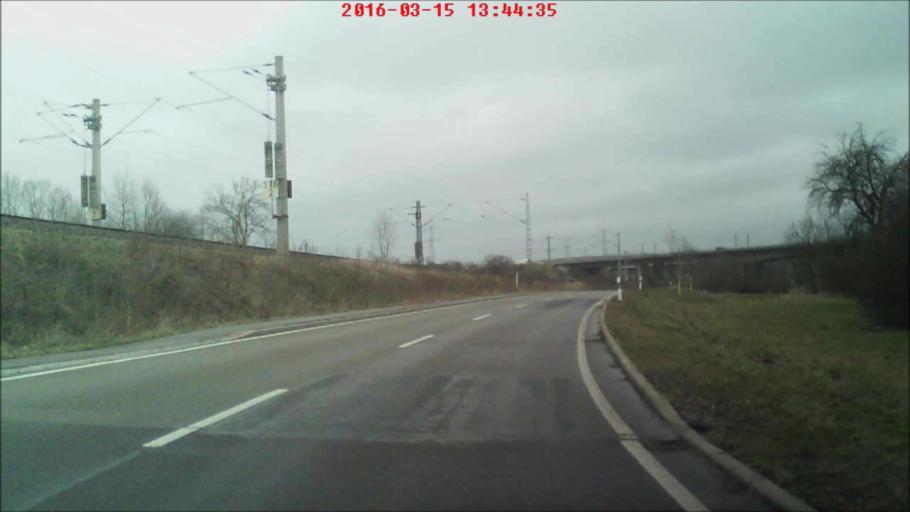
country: DE
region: Thuringia
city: Ingersleben
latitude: 50.9247
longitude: 10.9429
